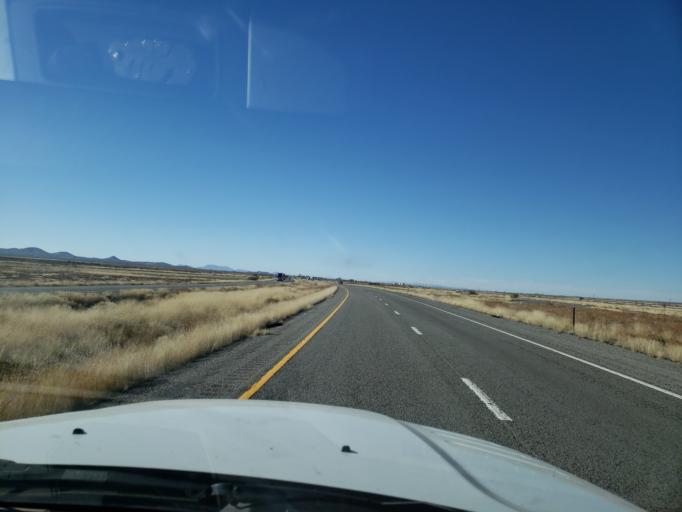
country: US
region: New Mexico
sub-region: Hidalgo County
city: Lordsburg
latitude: 32.3289
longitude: -108.6356
